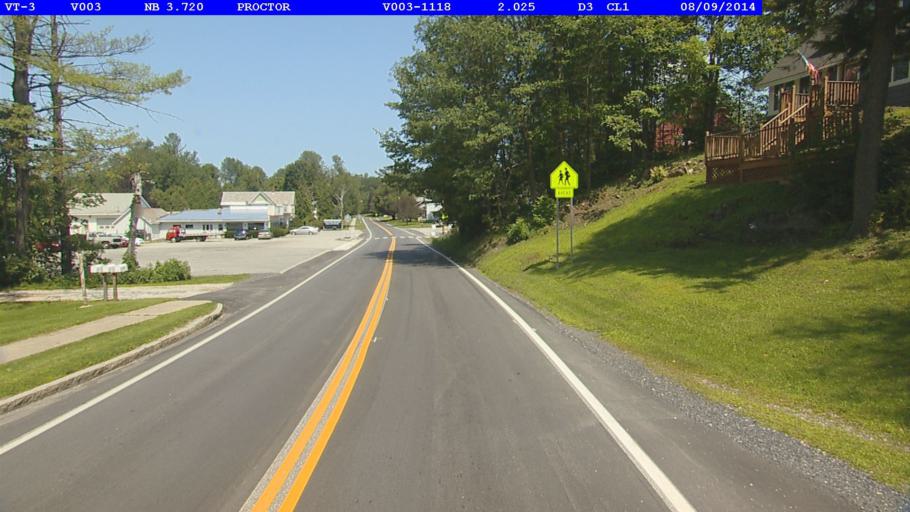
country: US
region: Vermont
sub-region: Rutland County
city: West Rutland
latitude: 43.6528
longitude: -73.0315
